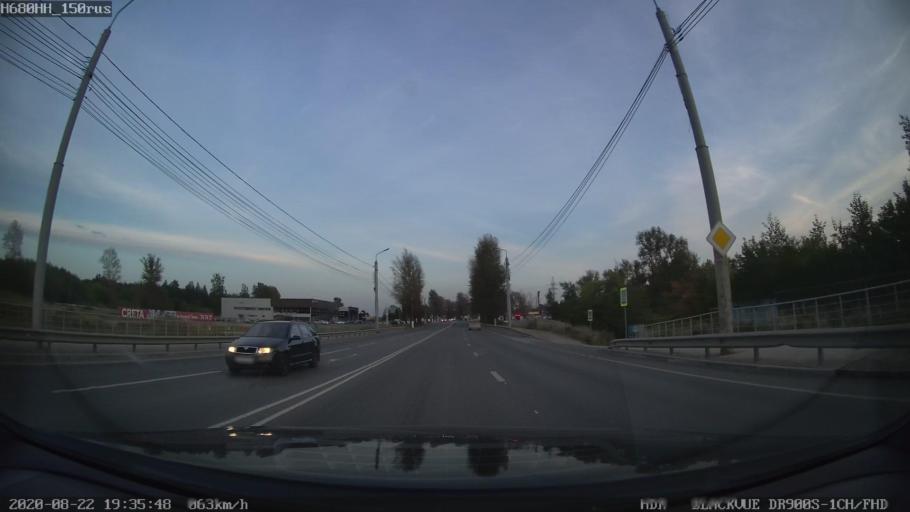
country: RU
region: Tverskaya
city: Tver
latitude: 56.8323
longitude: 35.9667
